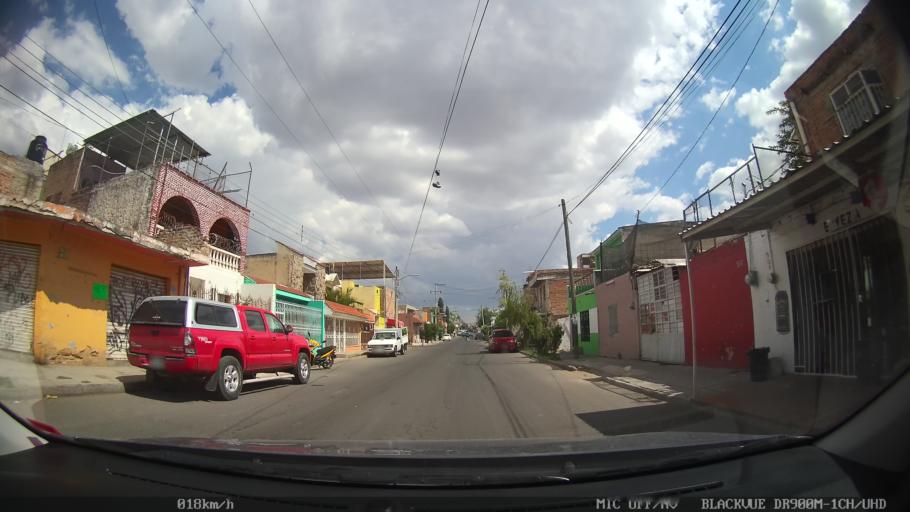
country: MX
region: Jalisco
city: Tlaquepaque
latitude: 20.6894
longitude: -103.2647
